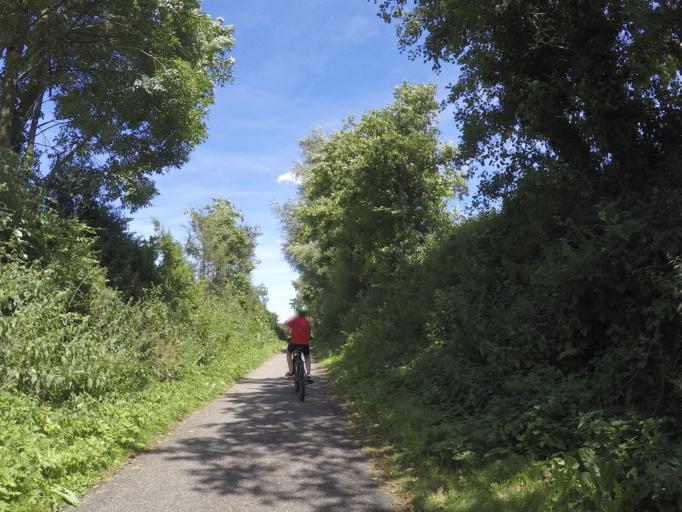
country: BE
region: Wallonia
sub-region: Province de Liege
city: Modave
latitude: 50.4090
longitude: 5.2941
